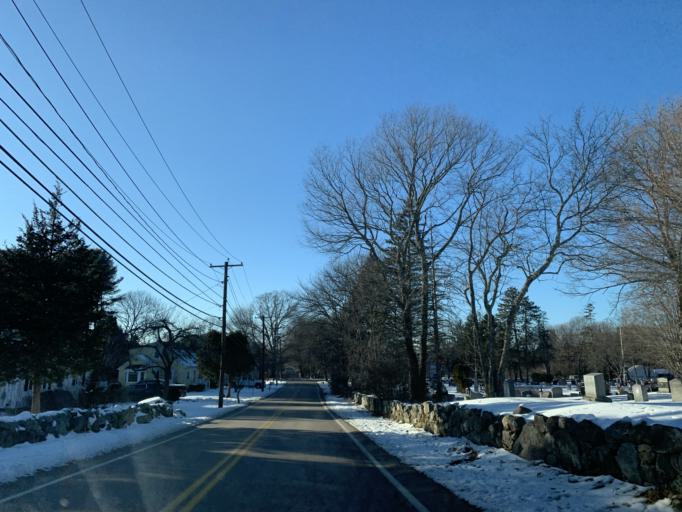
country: US
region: Massachusetts
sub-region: Norfolk County
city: Walpole
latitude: 42.1134
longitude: -71.2525
